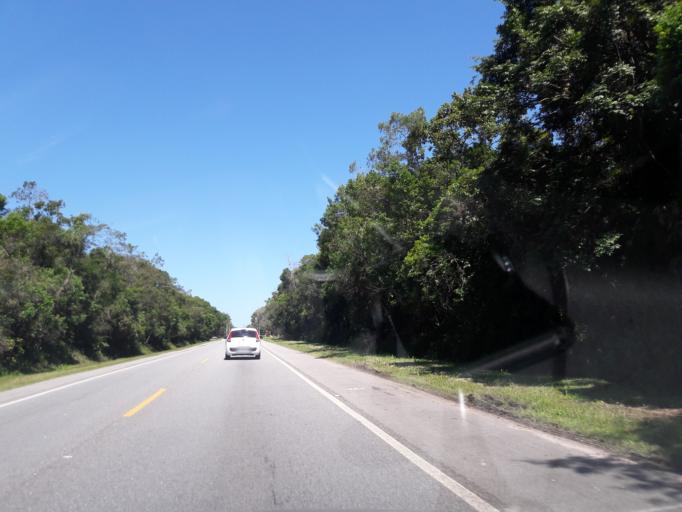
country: BR
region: Parana
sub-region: Pontal Do Parana
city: Pontal do Parana
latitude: -25.6347
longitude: -48.5369
